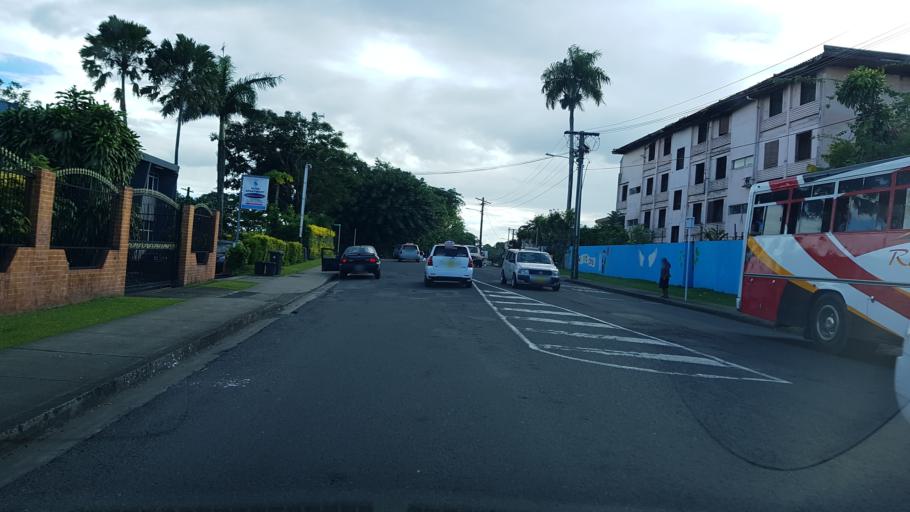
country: FJ
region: Central
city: Suva
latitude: -18.1459
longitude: 178.4331
